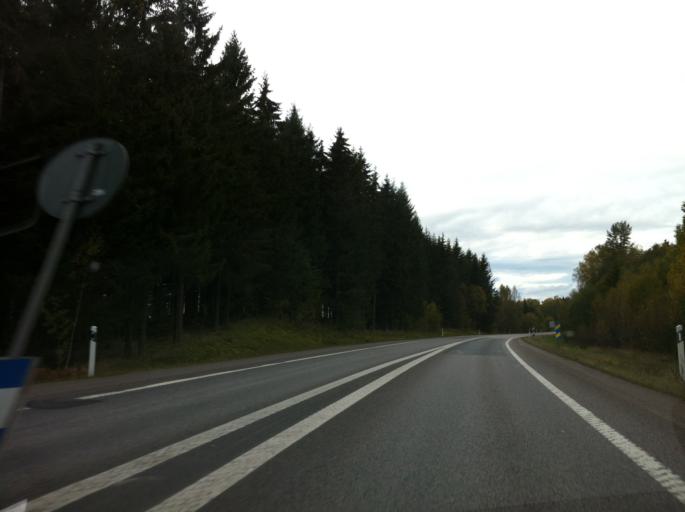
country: SE
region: OEstergoetland
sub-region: Motala Kommun
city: Motala
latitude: 58.6306
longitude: 14.9714
